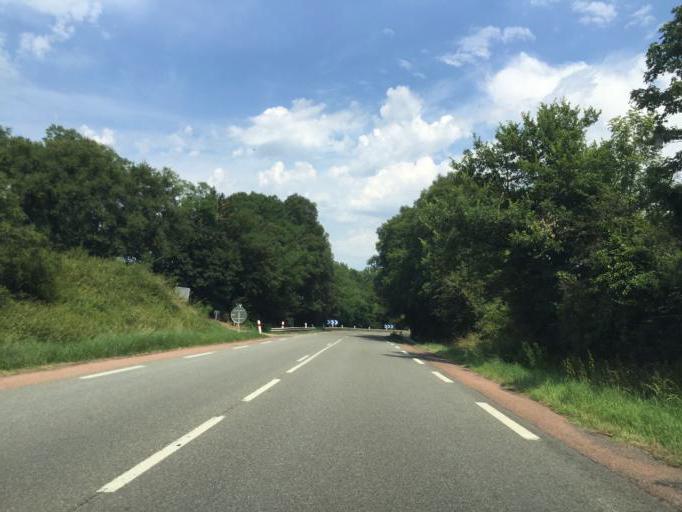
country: FR
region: Rhone-Alpes
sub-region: Departement du Rhone
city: Bully
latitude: 45.8458
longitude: 4.5873
